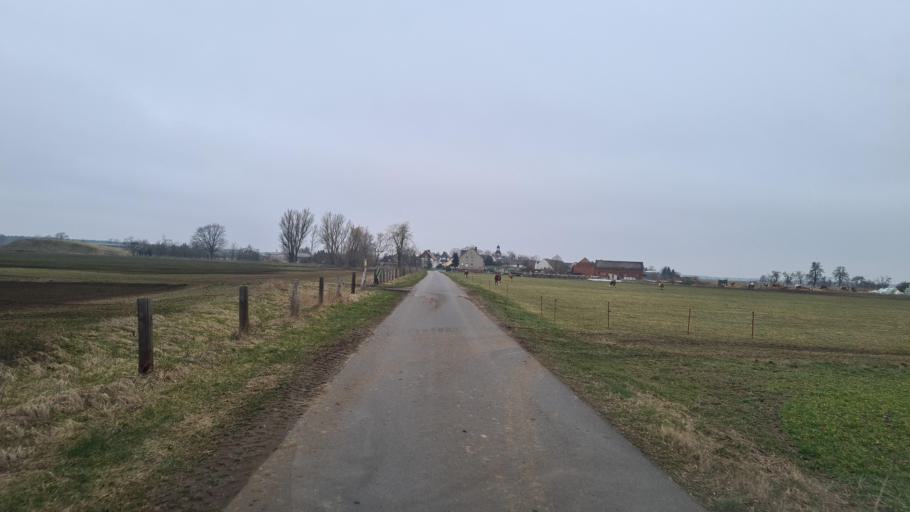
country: DE
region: Brandenburg
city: Herzberg
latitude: 51.6424
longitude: 13.1952
